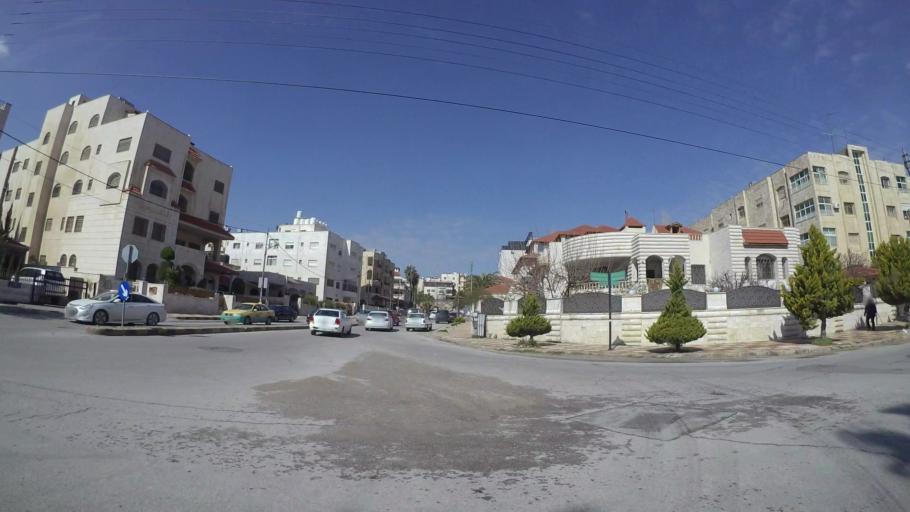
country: JO
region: Amman
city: Al Jubayhah
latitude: 31.9956
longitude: 35.8963
